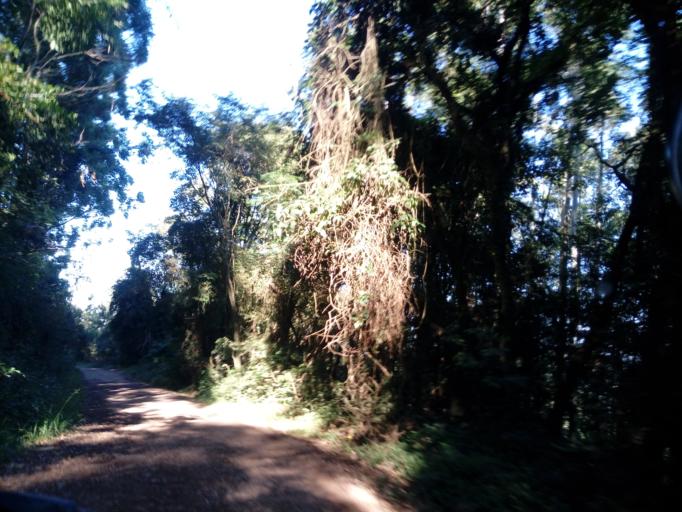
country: BR
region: Santa Catarina
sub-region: Chapeco
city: Chapeco
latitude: -27.1901
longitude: -52.7398
